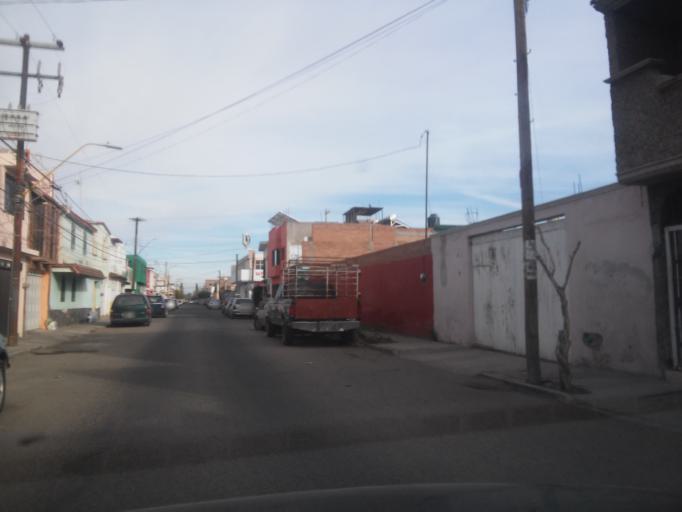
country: MX
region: Durango
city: Victoria de Durango
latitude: 24.0241
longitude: -104.6455
